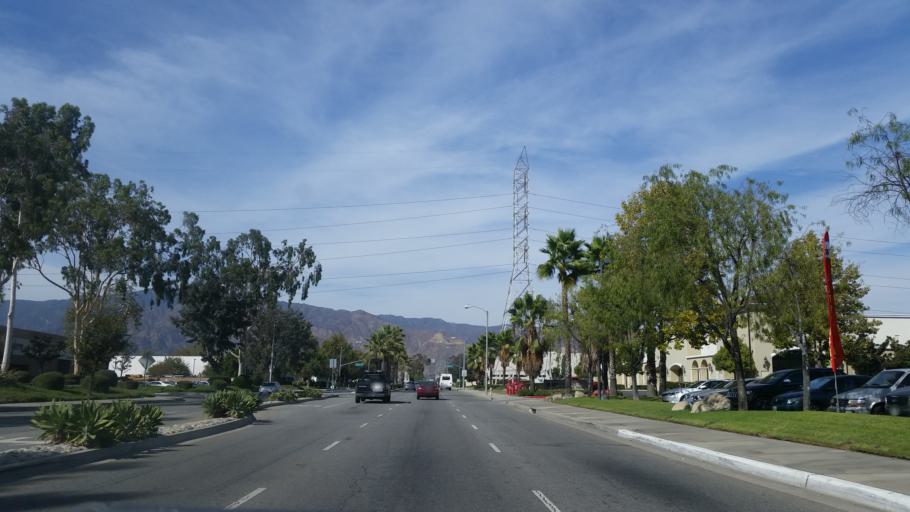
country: US
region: California
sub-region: Los Angeles County
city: Irwindale
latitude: 34.1094
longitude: -117.9341
